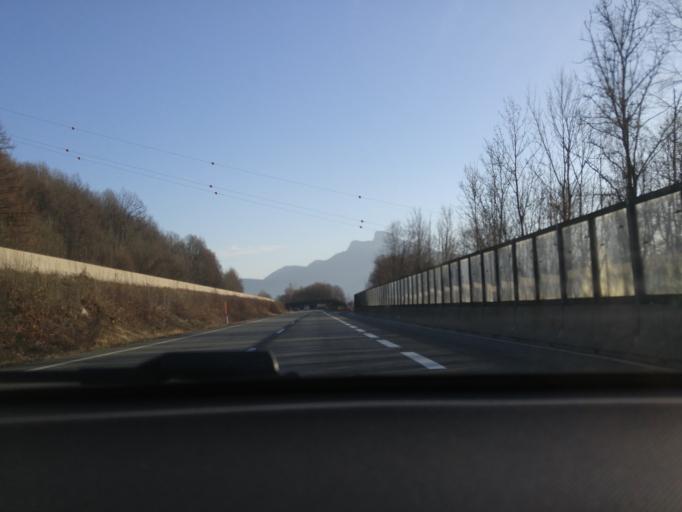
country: AT
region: Upper Austria
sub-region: Politischer Bezirk Vocklabruck
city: Mondsee
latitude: 47.8575
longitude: 13.3546
